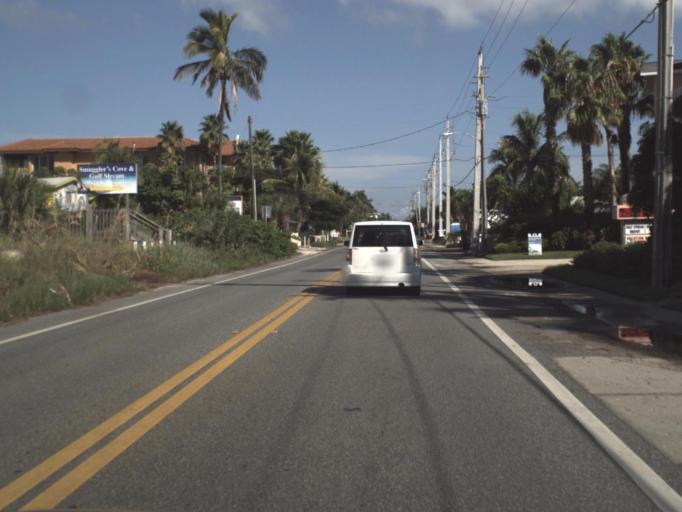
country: US
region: Florida
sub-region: Manatee County
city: Bradenton Beach
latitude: 27.4736
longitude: -82.7014
